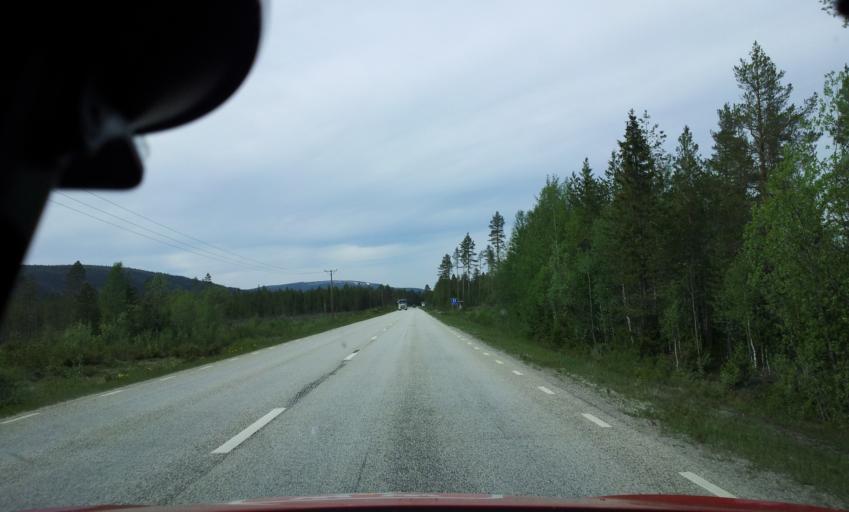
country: SE
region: Jaemtland
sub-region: Bergs Kommun
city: Hoverberg
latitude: 62.4977
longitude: 14.2095
